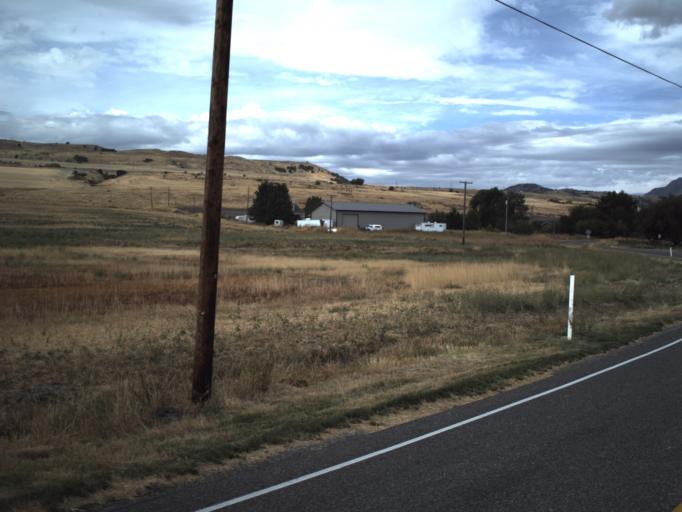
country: US
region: Utah
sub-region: Cache County
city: Benson
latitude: 41.8328
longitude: -112.0031
